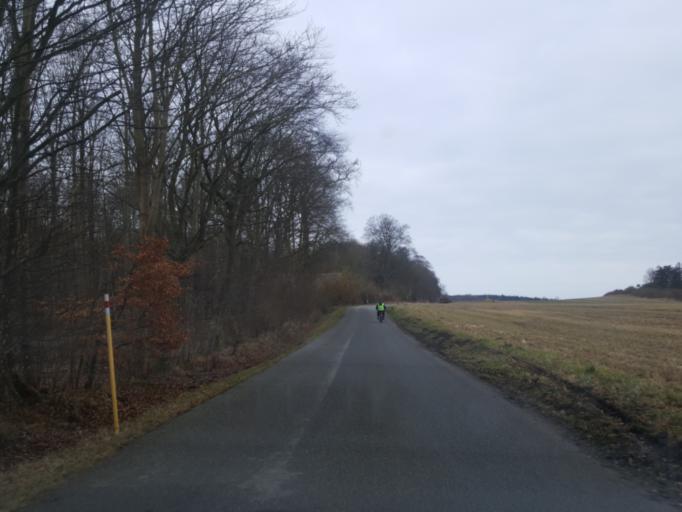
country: DK
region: Zealand
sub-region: Vordingborg Kommune
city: Neder Vindinge
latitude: 55.0356
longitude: 11.8357
